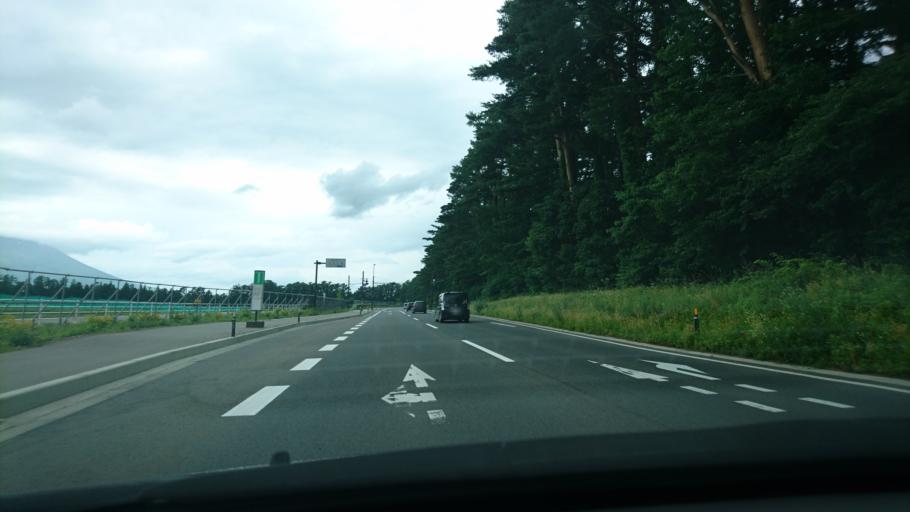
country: JP
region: Iwate
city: Morioka-shi
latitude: 39.7634
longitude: 141.1318
